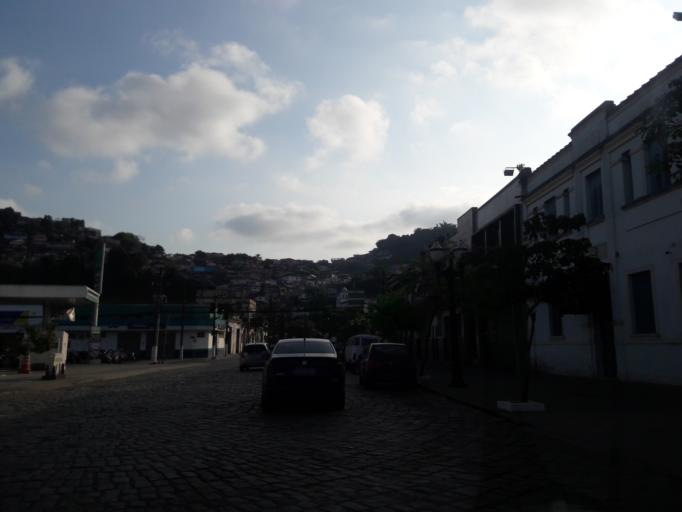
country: BR
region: Sao Paulo
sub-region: Santos
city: Santos
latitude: -23.9326
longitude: -46.3343
